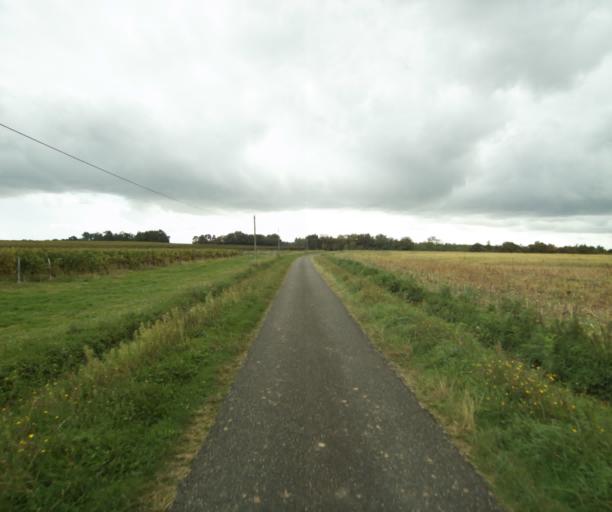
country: FR
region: Midi-Pyrenees
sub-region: Departement du Gers
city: Eauze
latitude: 43.8853
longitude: 0.0704
